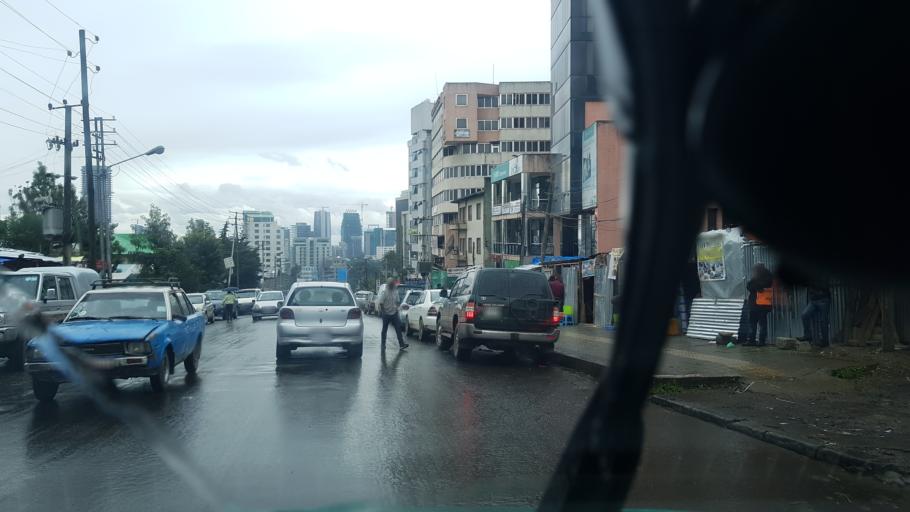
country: ET
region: Adis Abeba
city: Addis Ababa
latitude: 9.0294
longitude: 38.7523
